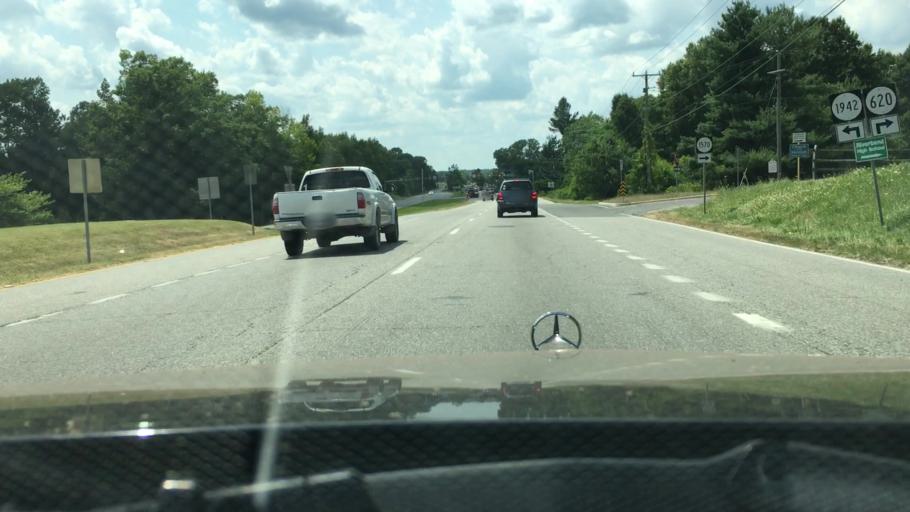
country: US
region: Virginia
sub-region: Spotsylvania County
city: Spotsylvania
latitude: 38.2922
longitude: -77.5734
